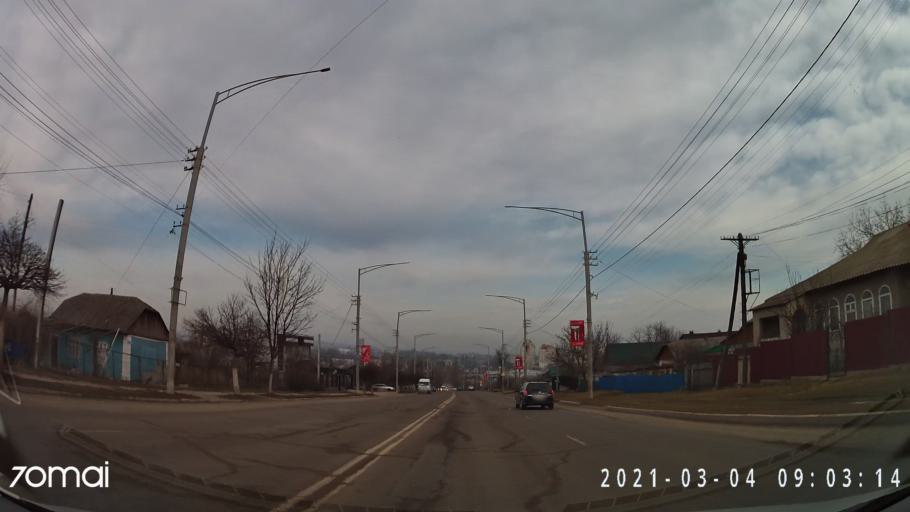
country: MD
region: Balti
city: Balti
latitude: 47.7480
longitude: 27.9463
